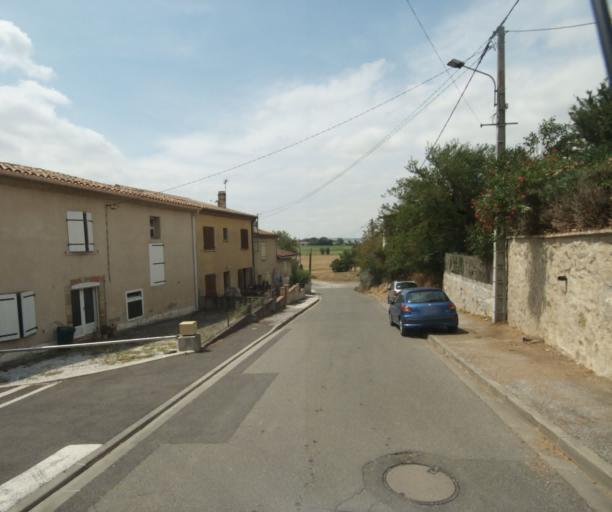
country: FR
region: Midi-Pyrenees
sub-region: Departement de la Haute-Garonne
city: Revel
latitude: 43.4362
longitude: 1.9665
